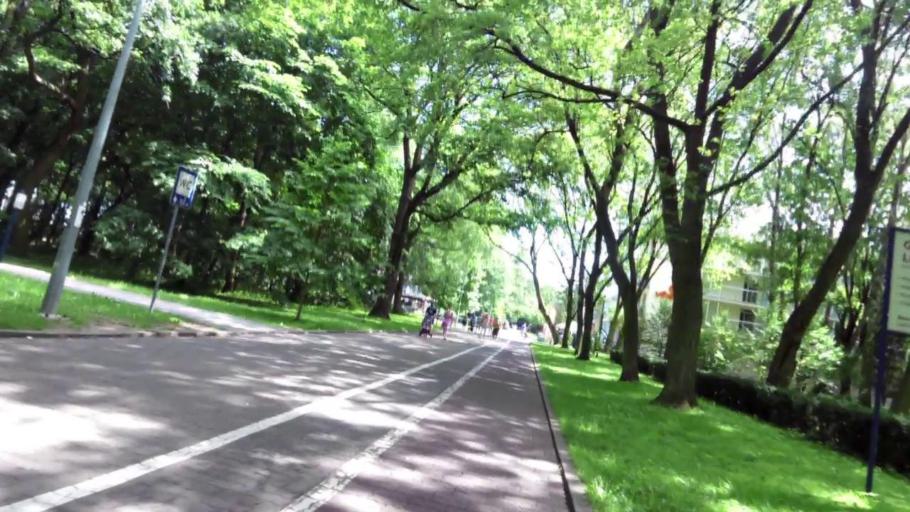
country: PL
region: West Pomeranian Voivodeship
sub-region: Powiat kolobrzeski
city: Kolobrzeg
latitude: 54.1855
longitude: 15.5830
